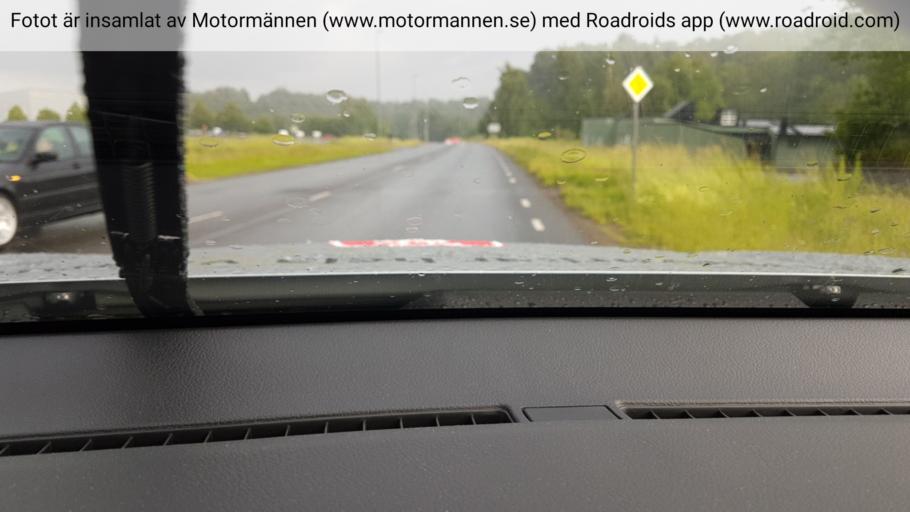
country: SE
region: Vaestra Goetaland
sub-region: Skovde Kommun
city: Skoevde
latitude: 58.4160
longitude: 13.8451
